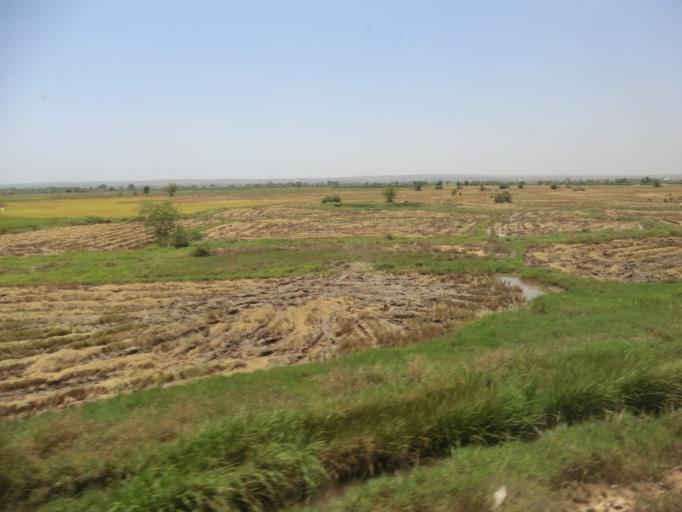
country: VN
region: Binh Thuan
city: Cho Lau
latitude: 11.2419
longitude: 108.4826
